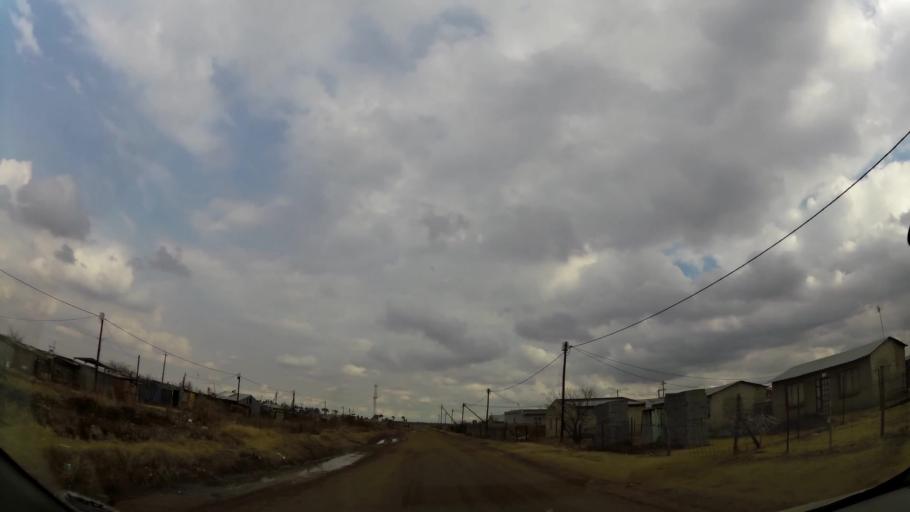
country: ZA
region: Orange Free State
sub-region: Fezile Dabi District Municipality
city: Sasolburg
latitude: -26.8641
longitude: 27.8946
